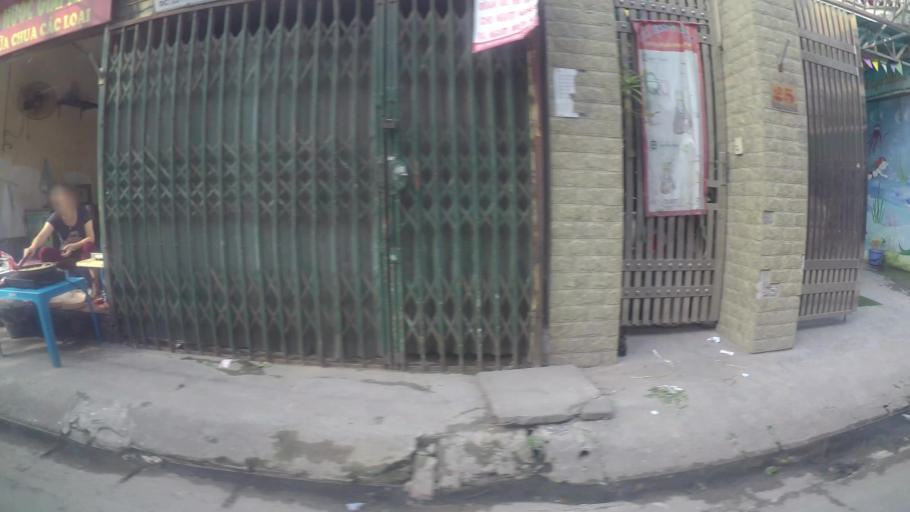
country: VN
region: Ha Noi
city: Tay Ho
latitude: 21.0520
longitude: 105.8097
